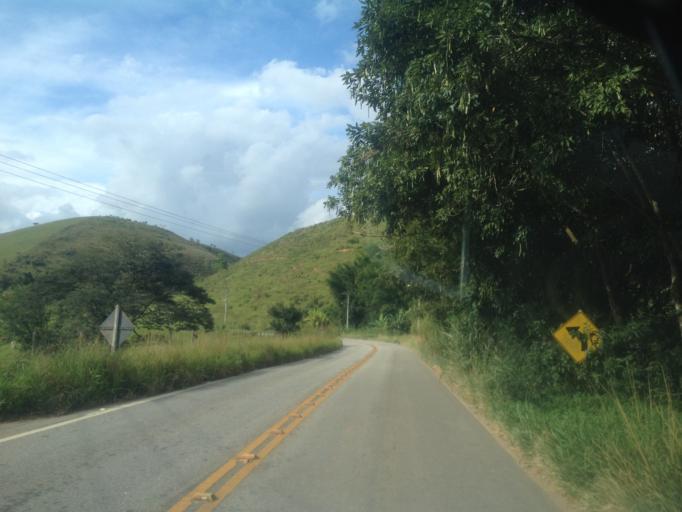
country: BR
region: Rio de Janeiro
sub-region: Quatis
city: Quatis
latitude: -22.3559
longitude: -44.2465
